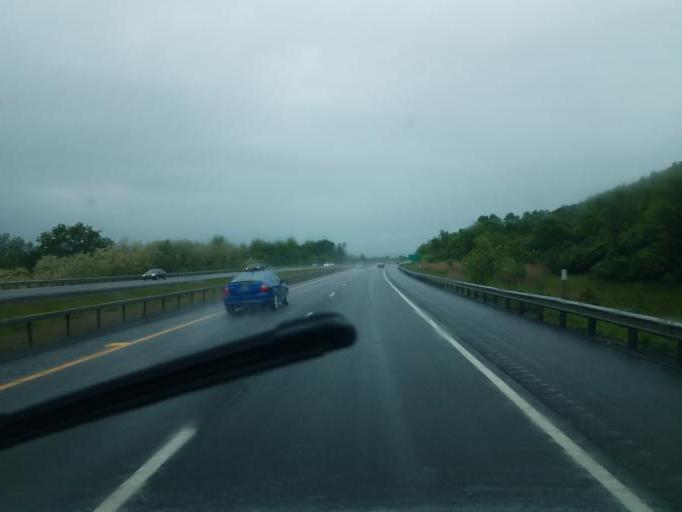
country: US
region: New York
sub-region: Herkimer County
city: Ilion
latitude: 43.0333
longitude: -75.0461
